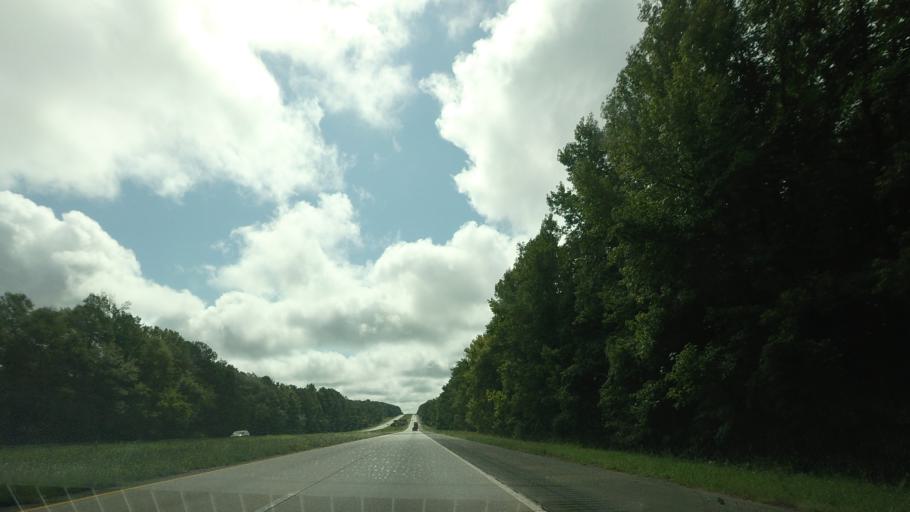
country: US
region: Georgia
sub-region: Houston County
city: Robins Air Force Base
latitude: 32.6750
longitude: -83.4780
